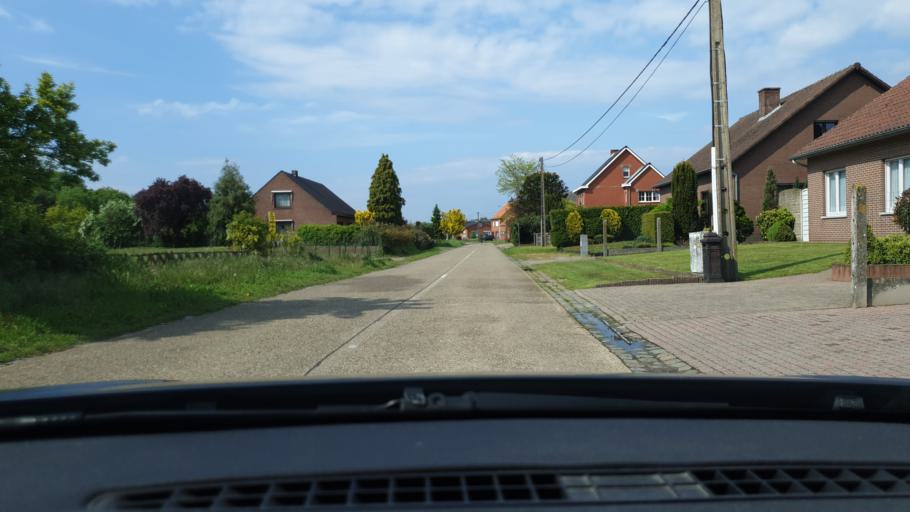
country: BE
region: Flanders
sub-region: Provincie Antwerpen
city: Meerhout
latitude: 51.1132
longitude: 5.1030
